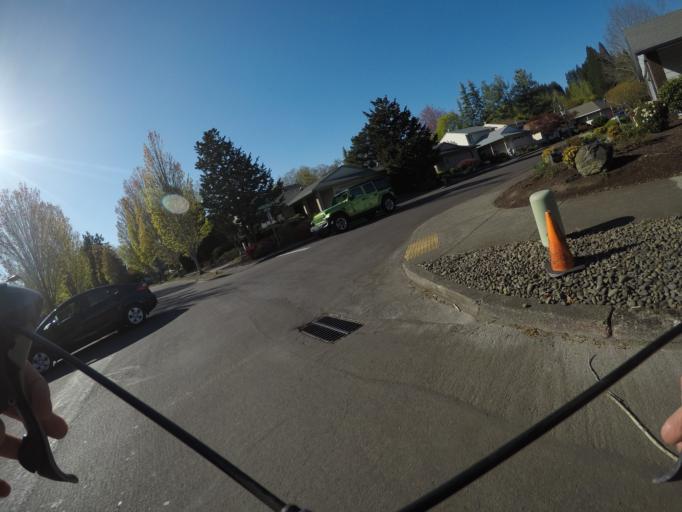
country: US
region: Oregon
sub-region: Washington County
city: King City
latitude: 45.4064
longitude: -122.7893
